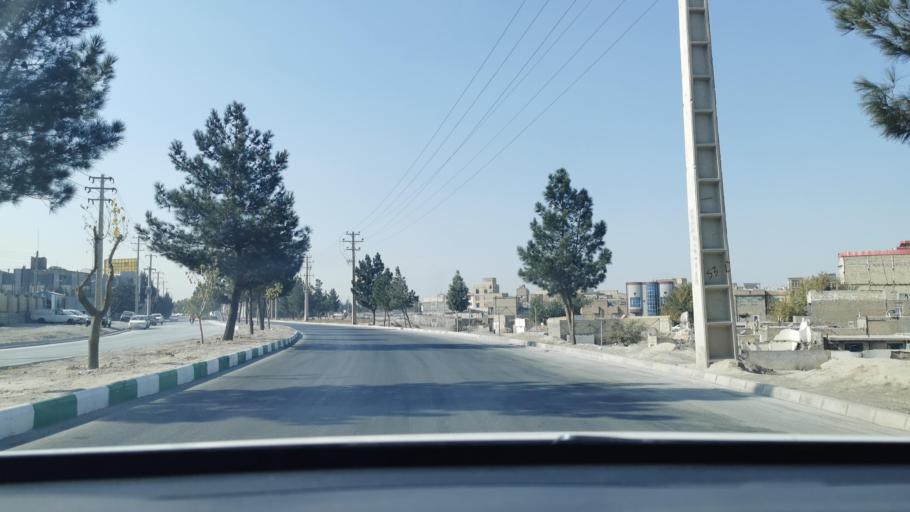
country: IR
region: Razavi Khorasan
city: Mashhad
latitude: 36.3486
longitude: 59.6021
